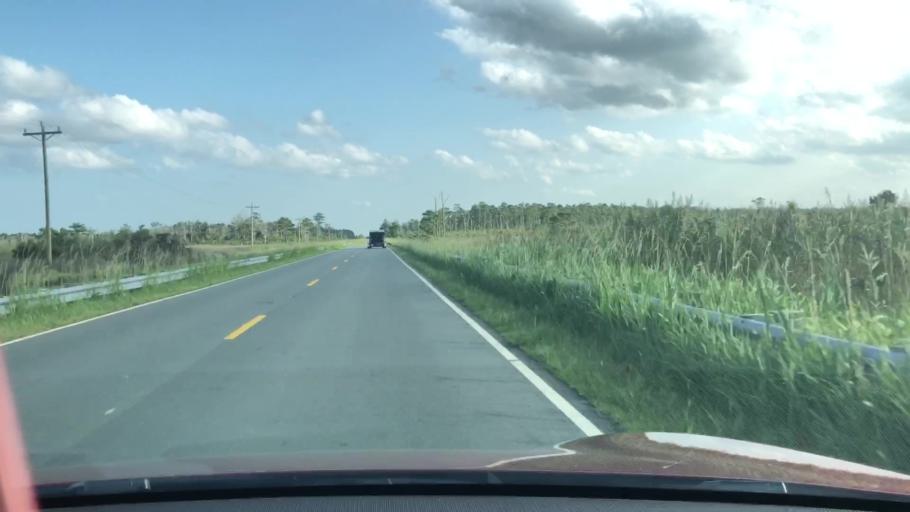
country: US
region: North Carolina
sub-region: Dare County
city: Wanchese
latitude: 35.6859
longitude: -75.7806
